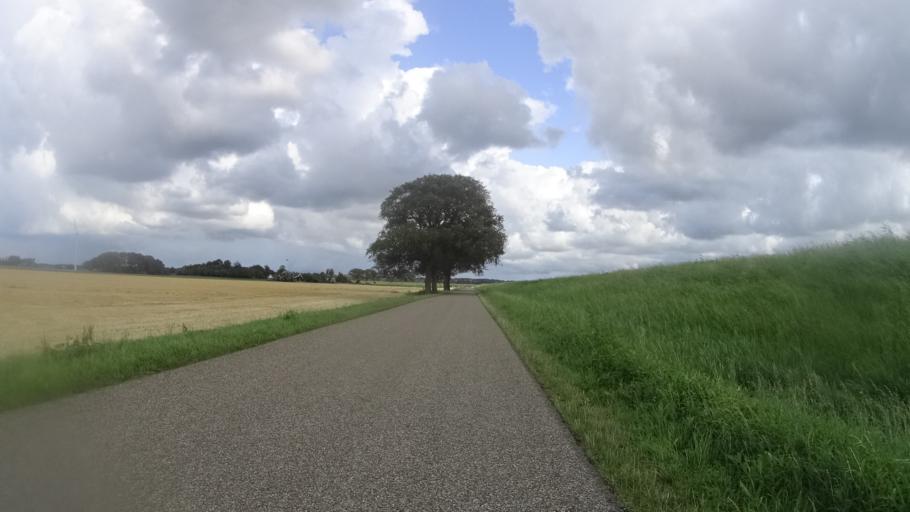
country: NL
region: North Holland
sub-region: Gemeente Schagen
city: Schagen
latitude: 52.8436
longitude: 4.8670
